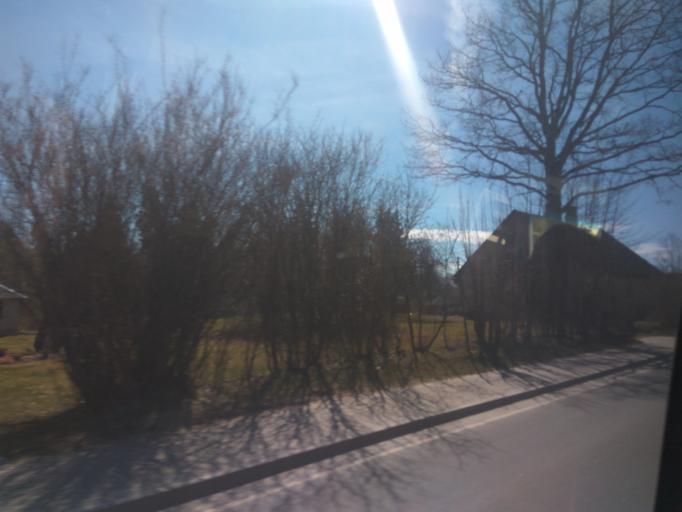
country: LV
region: Aluksnes Rajons
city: Aluksne
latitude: 57.4310
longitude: 27.0394
